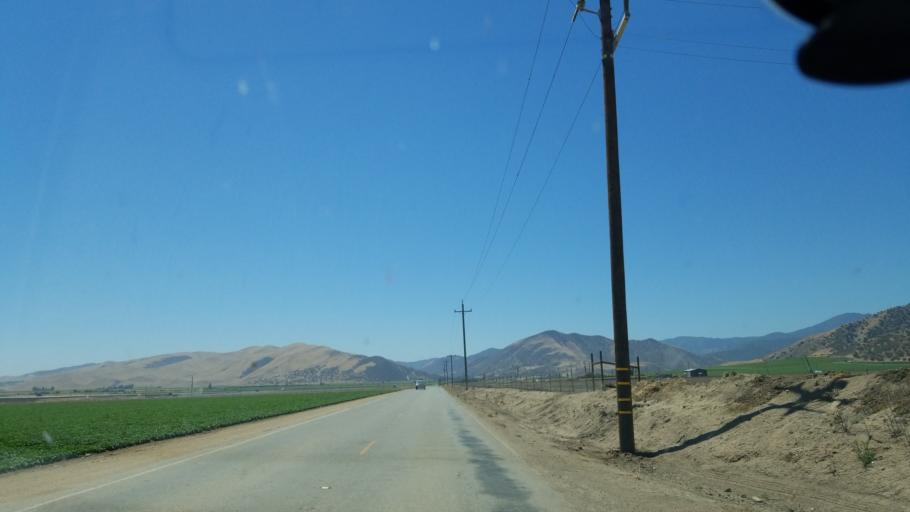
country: US
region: California
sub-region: Monterey County
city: Greenfield
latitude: 36.3325
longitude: -121.3160
